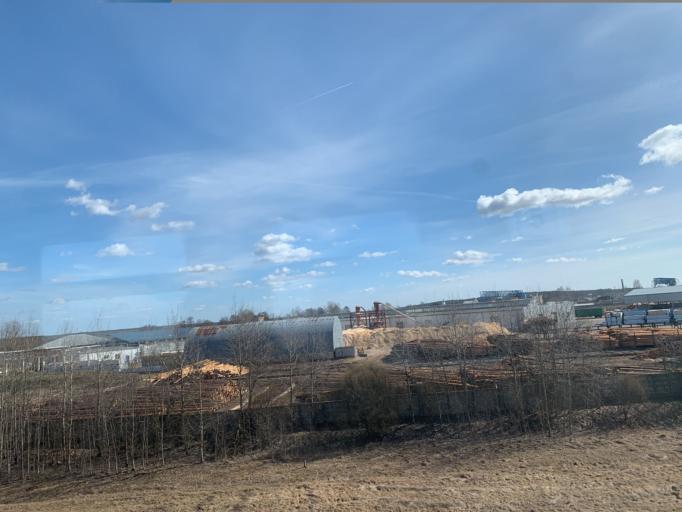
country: BY
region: Minsk
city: Novy Svyerzhan'
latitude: 53.4612
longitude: 26.7221
